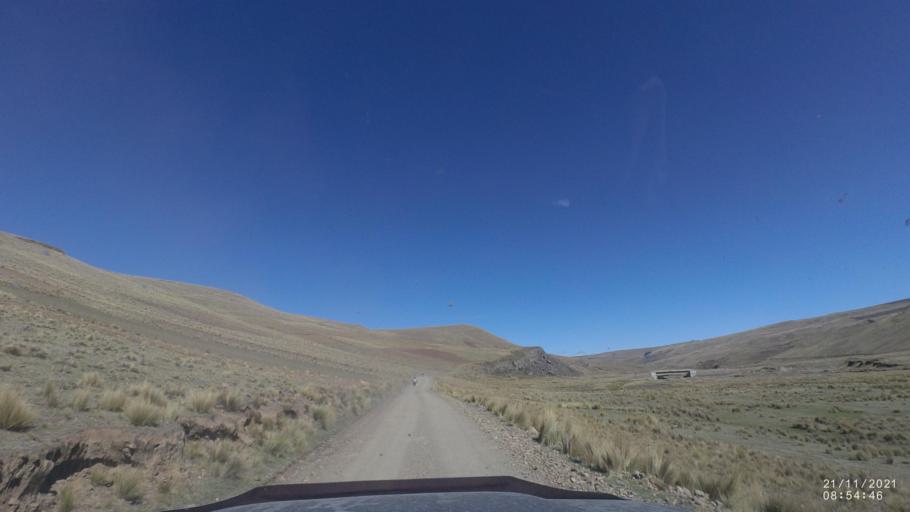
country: BO
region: Cochabamba
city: Cochabamba
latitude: -17.2016
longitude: -66.2449
